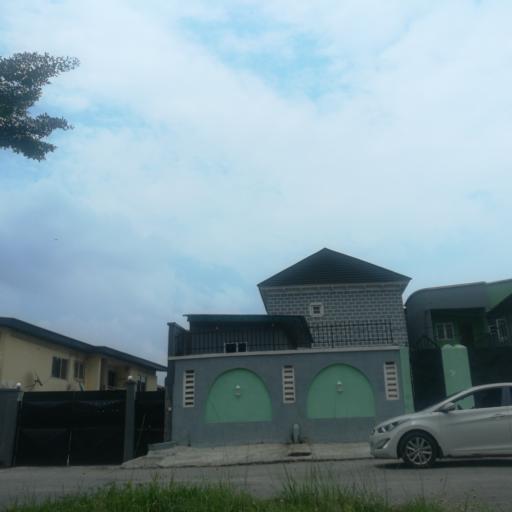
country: NG
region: Lagos
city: Ojota
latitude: 6.5766
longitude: 3.3799
